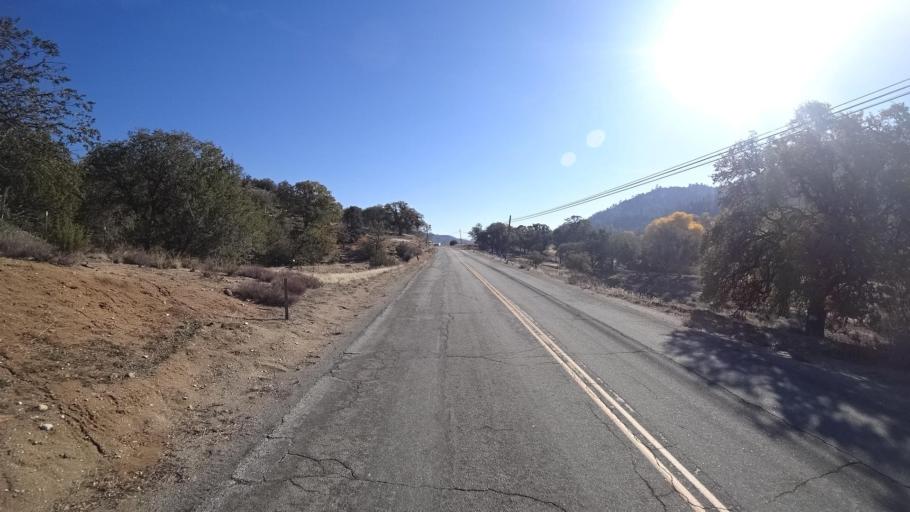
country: US
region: California
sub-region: Kern County
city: Bodfish
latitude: 35.3974
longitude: -118.4518
